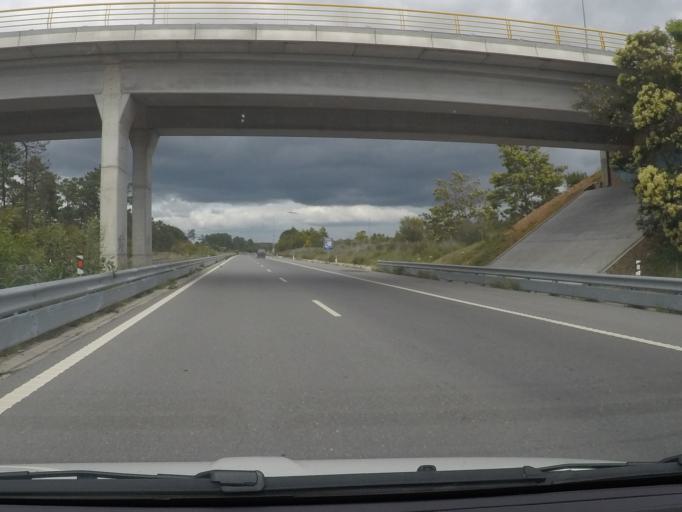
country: PT
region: Setubal
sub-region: Santiago do Cacem
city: Santo Andre
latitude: 37.9837
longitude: -8.7852
